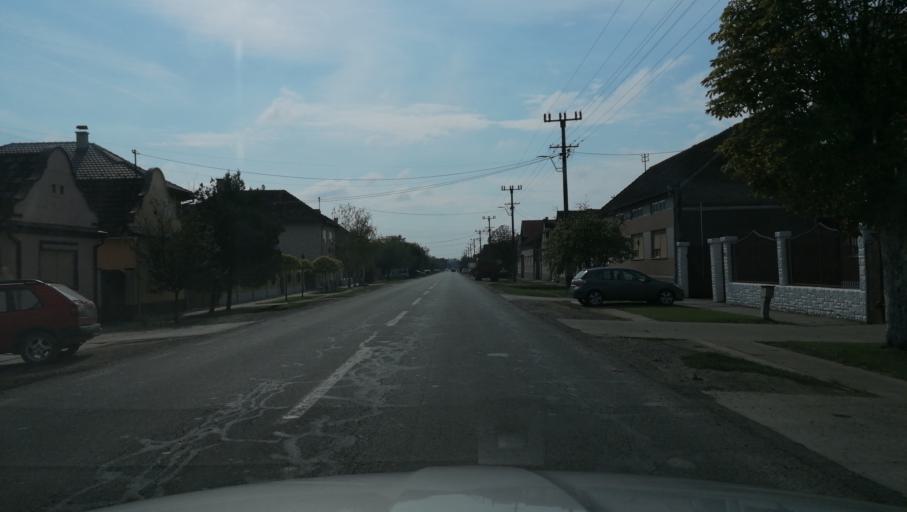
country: RS
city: Ravnje
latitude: 45.0214
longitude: 19.4022
